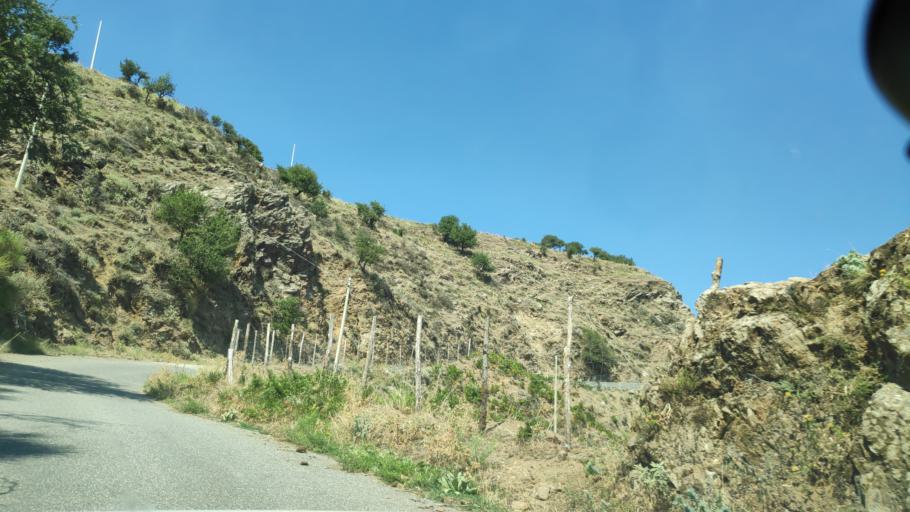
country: IT
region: Calabria
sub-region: Provincia di Reggio Calabria
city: Bova
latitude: 38.0098
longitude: 15.9330
